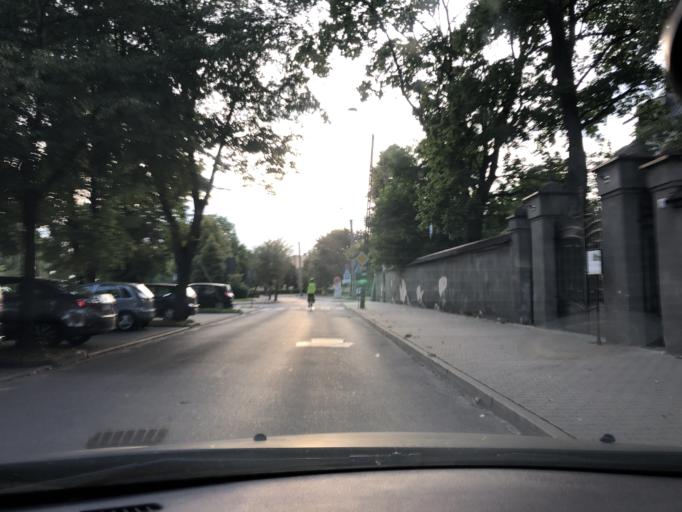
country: PL
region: Lodz Voivodeship
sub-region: Powiat wielunski
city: Wielun
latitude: 51.2224
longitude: 18.5708
